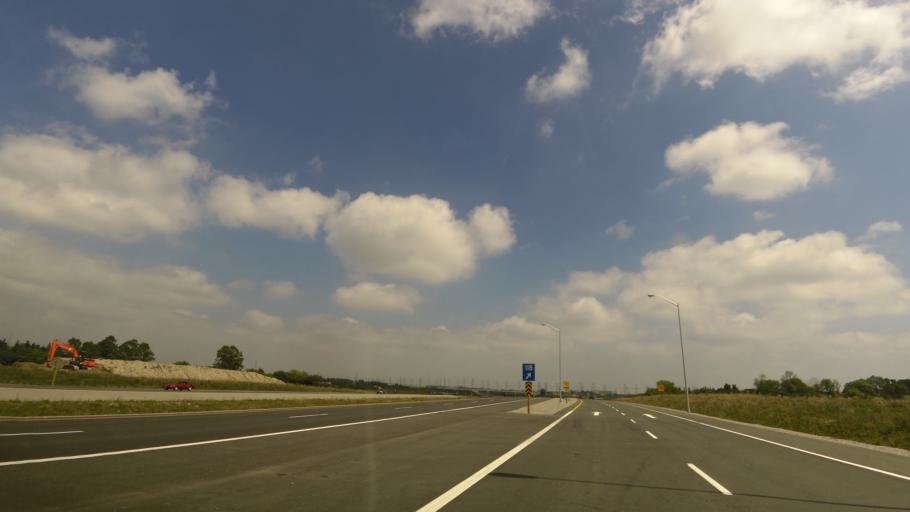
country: CA
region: Ontario
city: Ajax
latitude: 43.9478
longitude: -78.9683
